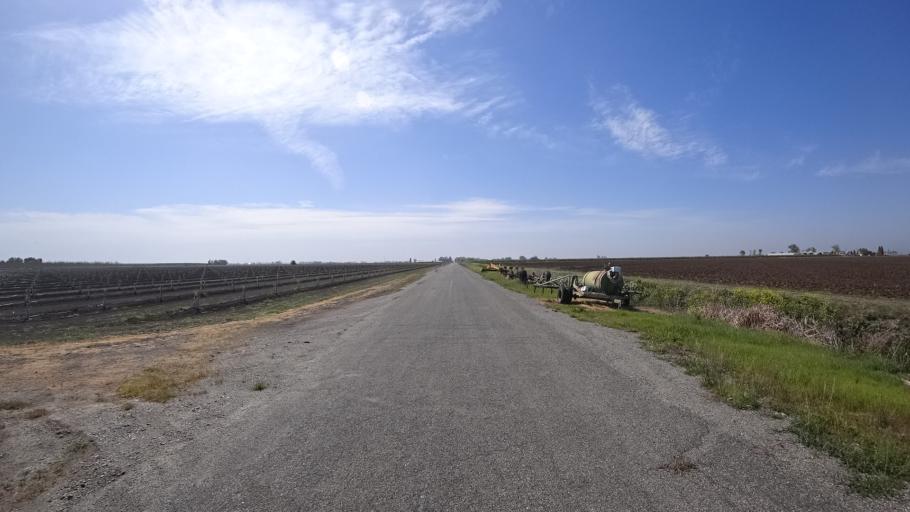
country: US
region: California
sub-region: Glenn County
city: Hamilton City
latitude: 39.6197
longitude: -122.0556
